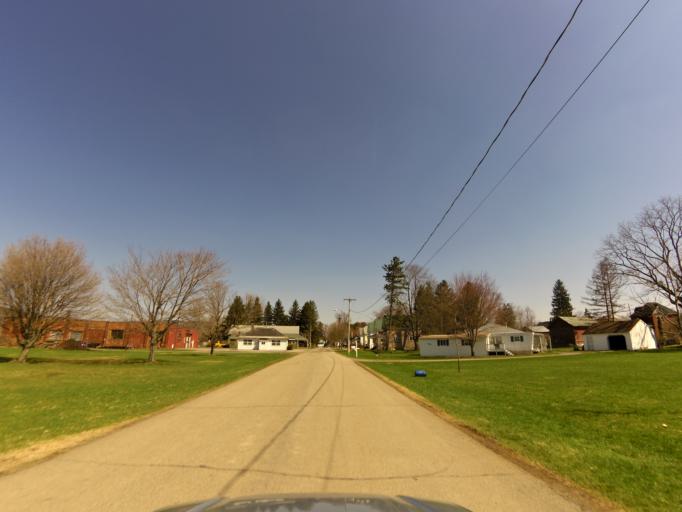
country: US
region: New York
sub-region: Cattaraugus County
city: Franklinville
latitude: 42.3315
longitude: -78.4614
